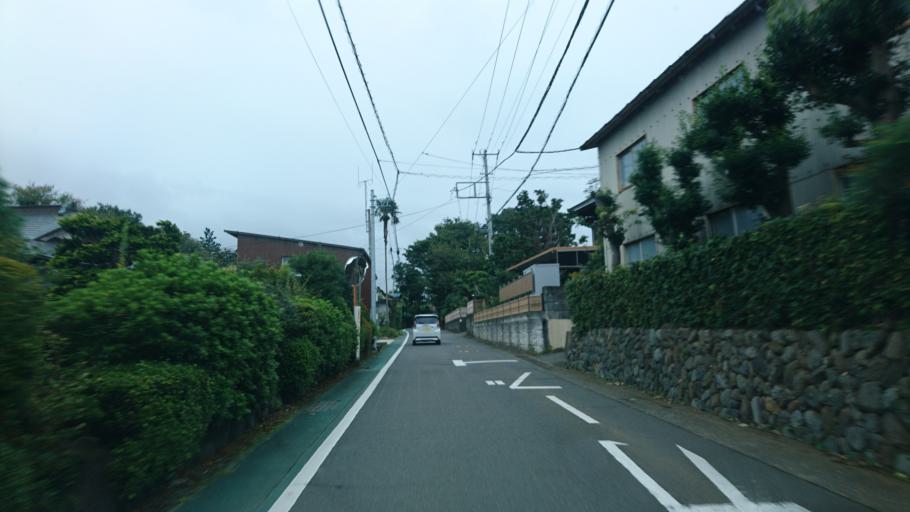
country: JP
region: Kanagawa
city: Atsugi
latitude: 35.4868
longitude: 139.3237
